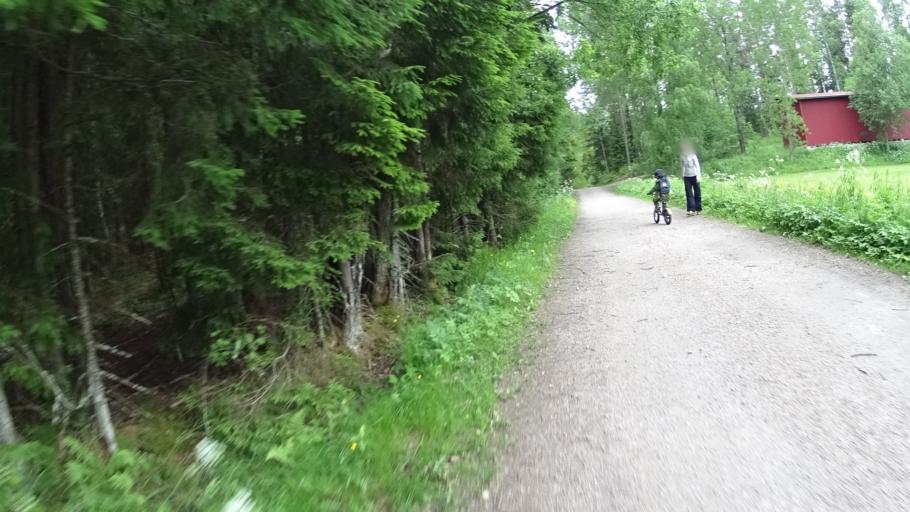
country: FI
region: Uusimaa
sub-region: Helsinki
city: Espoo
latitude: 60.2685
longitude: 24.6502
